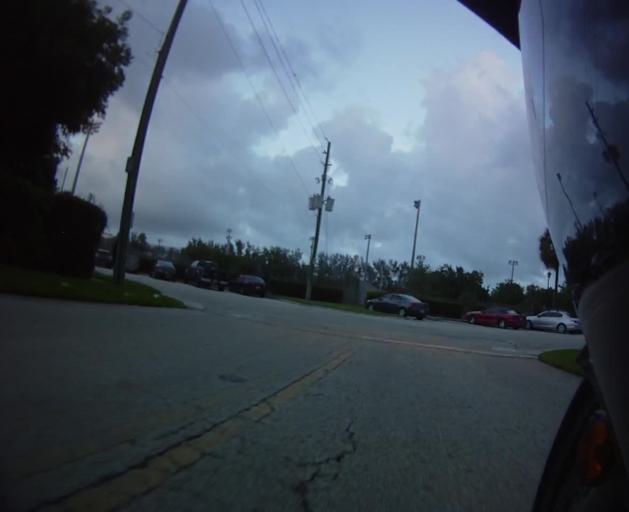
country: US
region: Florida
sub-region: Miami-Dade County
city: Miami Beach
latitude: 25.7853
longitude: -80.1388
